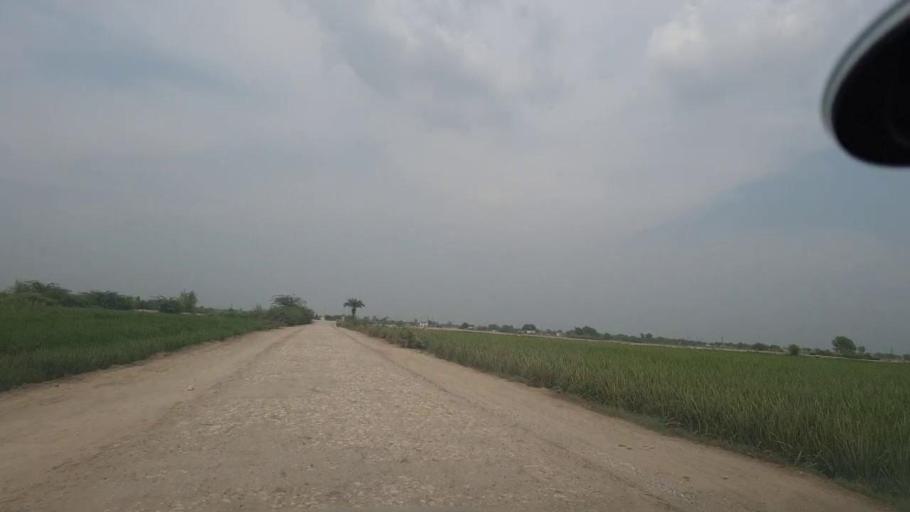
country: PK
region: Sindh
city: Jacobabad
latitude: 28.2512
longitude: 68.4368
